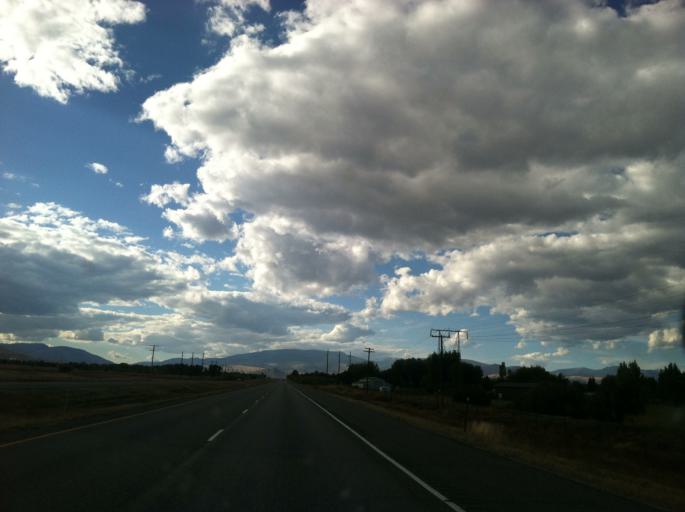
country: US
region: Montana
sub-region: Deer Lodge County
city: Warm Springs
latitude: 46.1004
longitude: -112.8343
